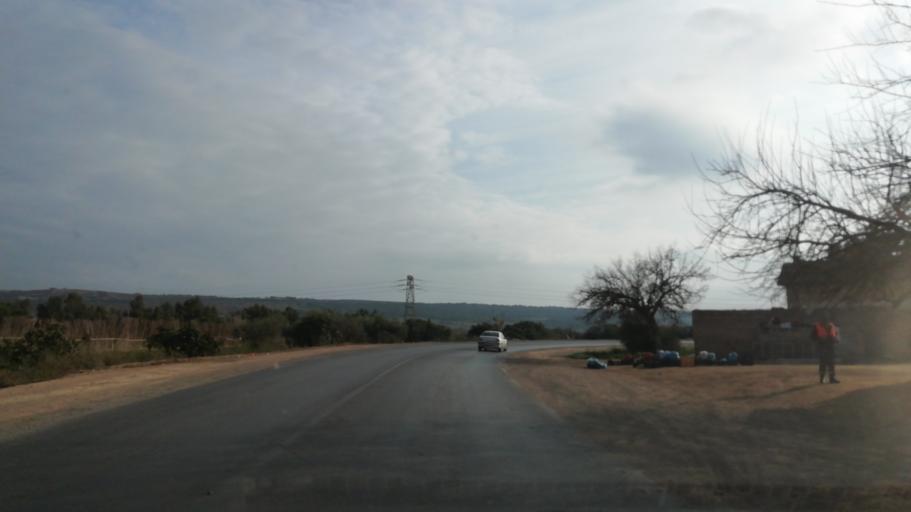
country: DZ
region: Mostaganem
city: Mostaganem
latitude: 35.8473
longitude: 0.0701
